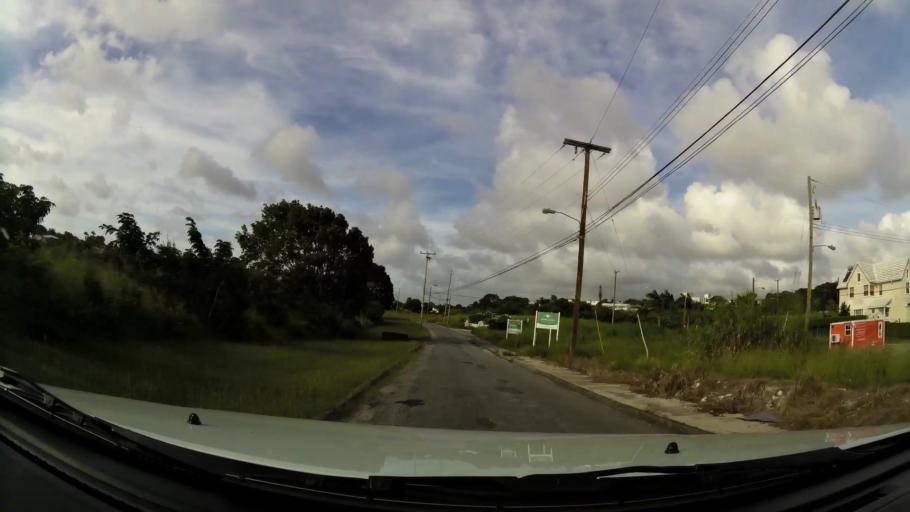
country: BB
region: Christ Church
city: Oistins
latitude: 13.0914
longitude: -59.5699
